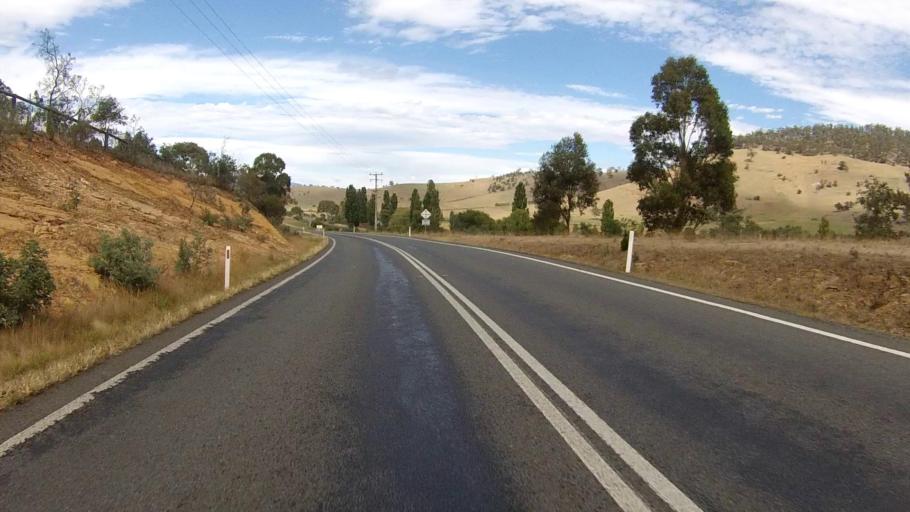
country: AU
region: Tasmania
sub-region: Brighton
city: Old Beach
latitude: -42.6713
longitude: 147.3633
